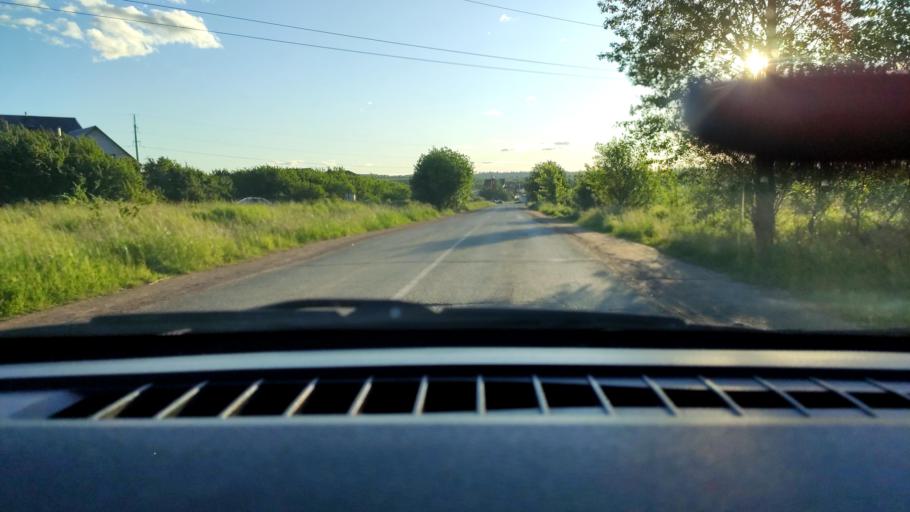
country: RU
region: Perm
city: Kultayevo
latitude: 57.9287
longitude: 55.8674
